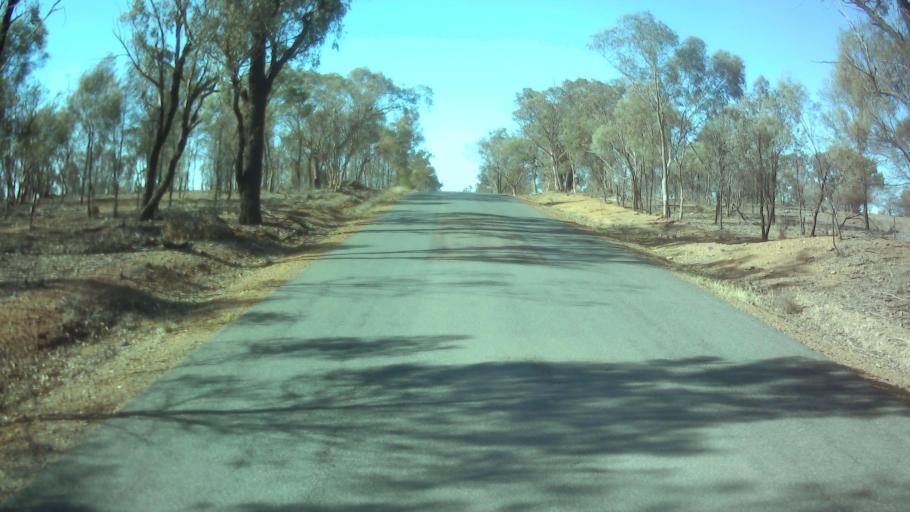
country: AU
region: New South Wales
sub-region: Forbes
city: Forbes
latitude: -33.7056
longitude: 147.8057
